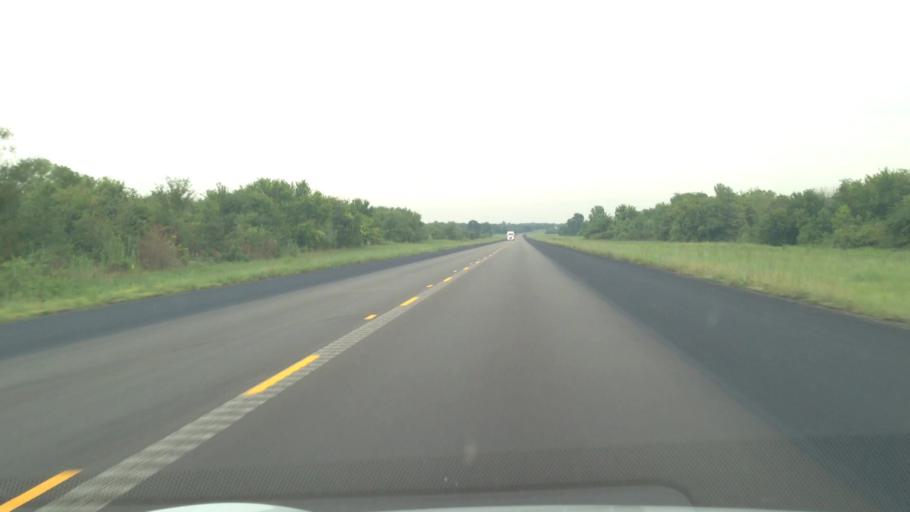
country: US
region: Kansas
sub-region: Cherokee County
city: Baxter Springs
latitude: 37.0385
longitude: -94.7087
